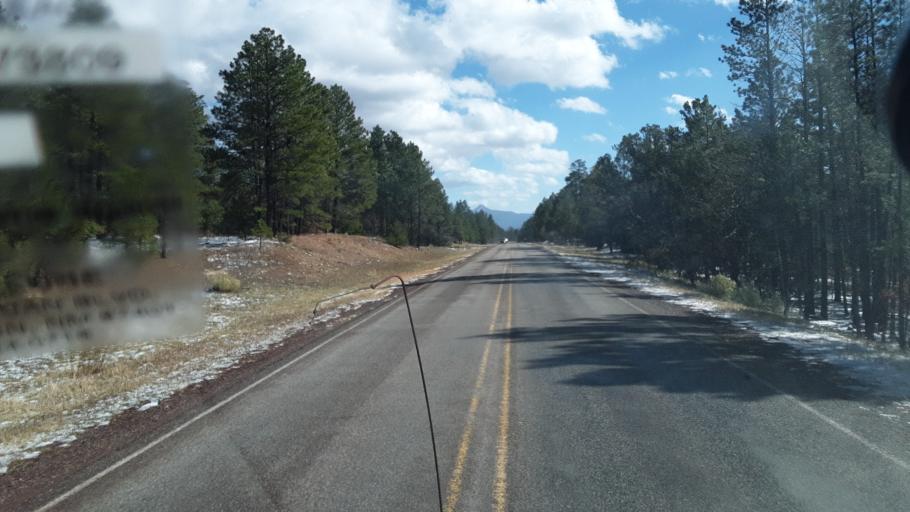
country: US
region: New Mexico
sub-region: Rio Arriba County
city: Santa Teresa
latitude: 36.2001
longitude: -106.7596
